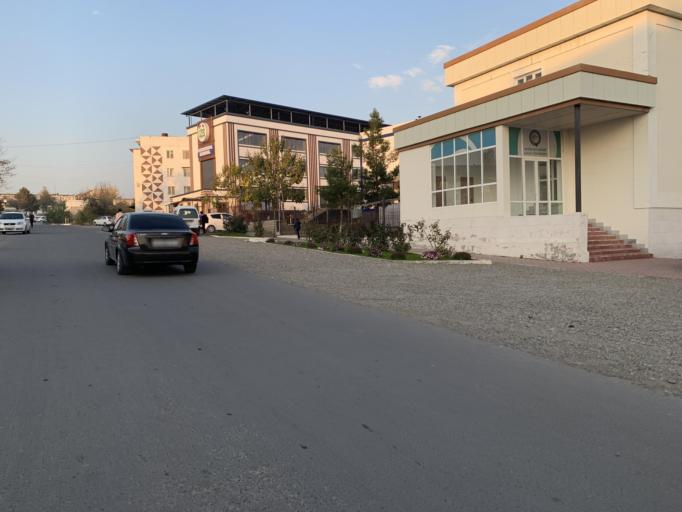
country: UZ
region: Namangan
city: Namangan Shahri
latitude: 41.0026
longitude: 71.5988
